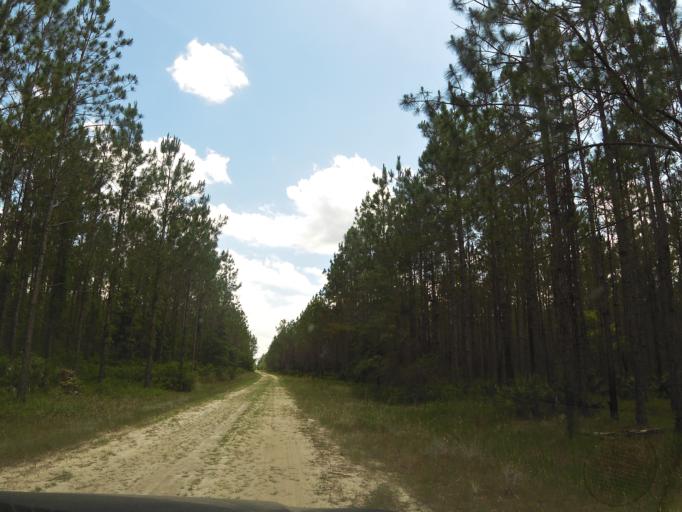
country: US
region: Florida
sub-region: Clay County
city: Keystone Heights
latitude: 29.8591
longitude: -81.8539
